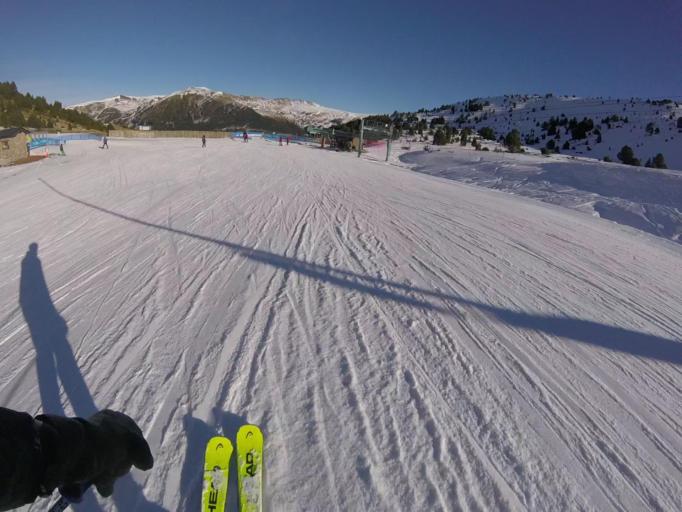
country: AD
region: Canillo
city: El Tarter
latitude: 42.5532
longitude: 1.6621
